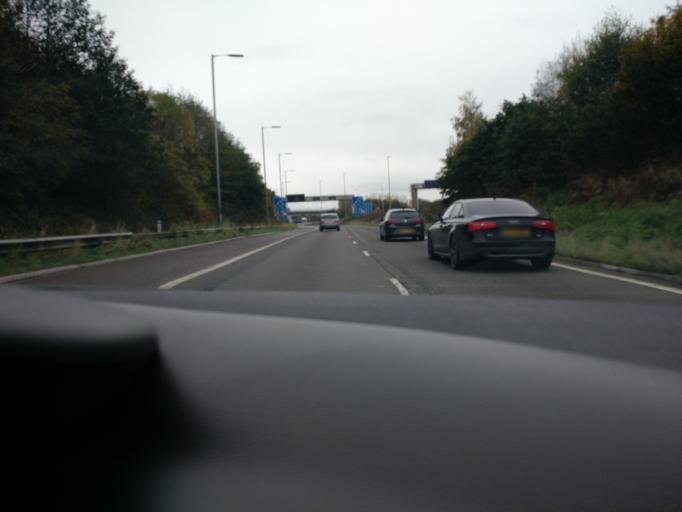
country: GB
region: England
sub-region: Lancashire
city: Goosnargh
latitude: 53.8051
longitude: -2.6945
